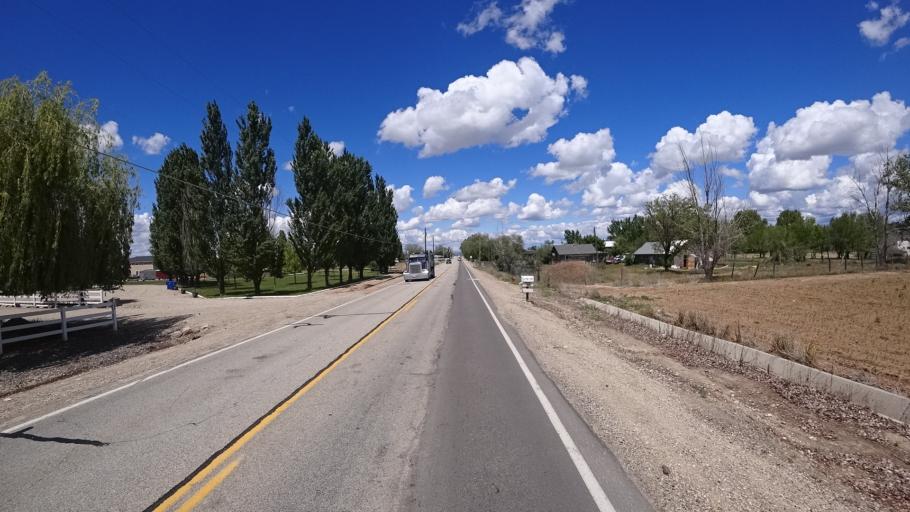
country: US
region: Idaho
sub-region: Ada County
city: Meridian
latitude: 43.5790
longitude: -116.4338
